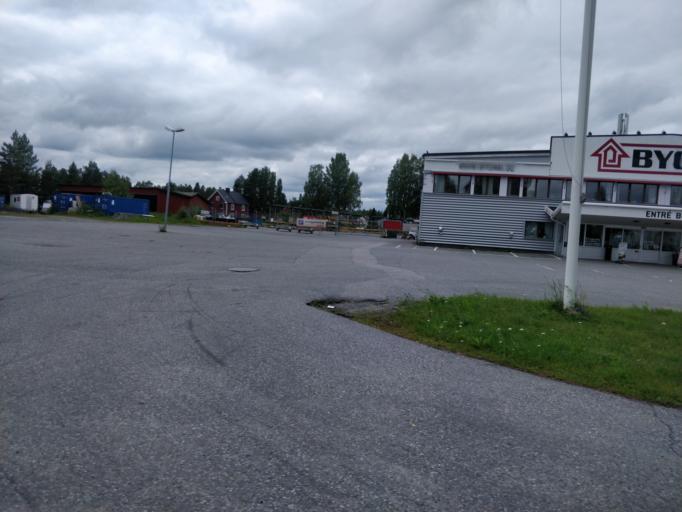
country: SE
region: Vaesterbotten
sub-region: Skelleftea Kommun
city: Viken
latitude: 64.7591
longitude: 20.8899
